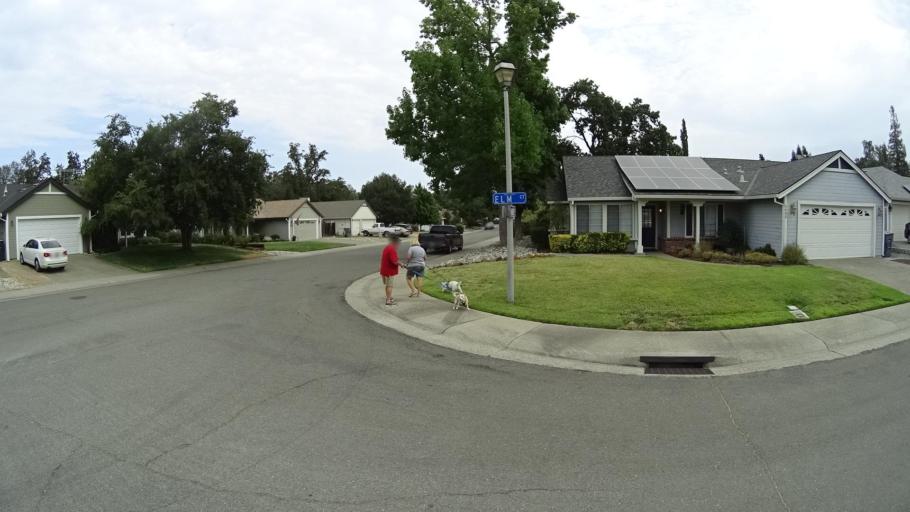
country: US
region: California
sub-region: Placer County
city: Loomis
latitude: 38.8087
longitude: -121.2018
